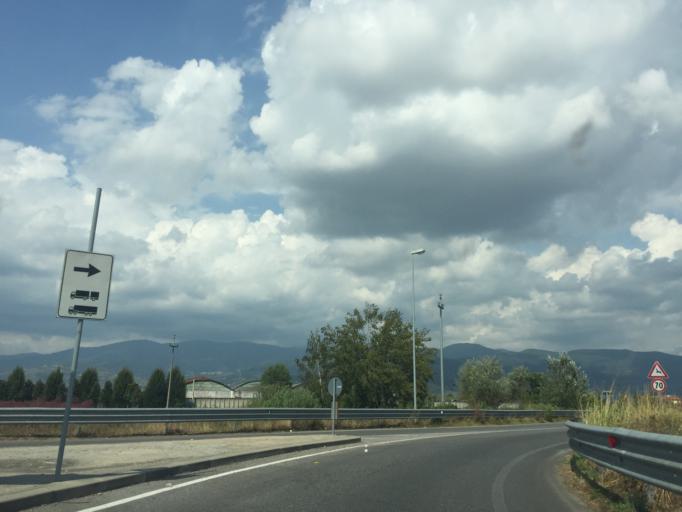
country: IT
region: Tuscany
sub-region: Provincia di Pistoia
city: Pistoia
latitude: 43.9131
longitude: 10.9366
